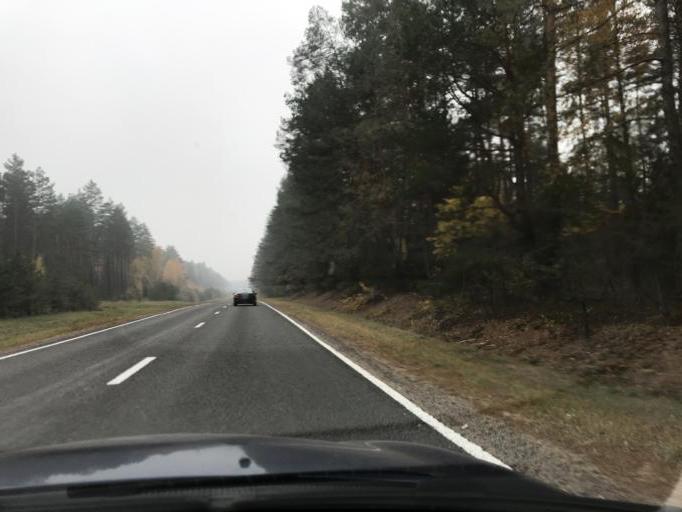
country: LT
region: Alytaus apskritis
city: Druskininkai
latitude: 53.8812
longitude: 23.9037
